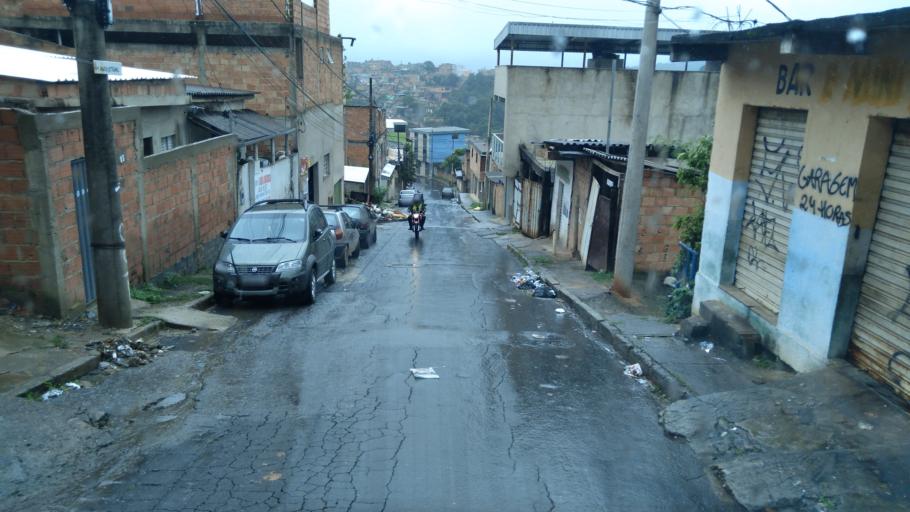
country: BR
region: Minas Gerais
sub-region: Belo Horizonte
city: Belo Horizonte
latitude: -19.9184
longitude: -43.8767
